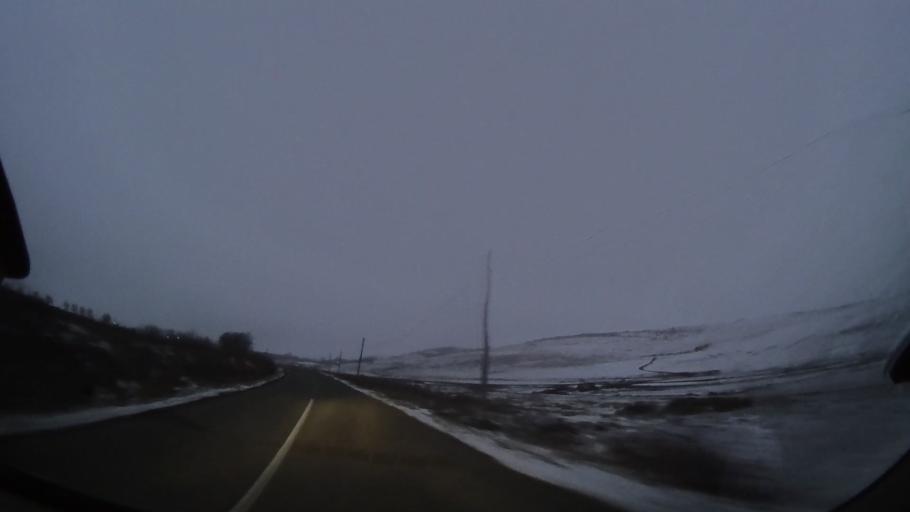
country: RO
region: Vaslui
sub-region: Comuna Dimitrie Cantemir
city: Dimitrie Cantemir
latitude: 46.4907
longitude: 28.0542
